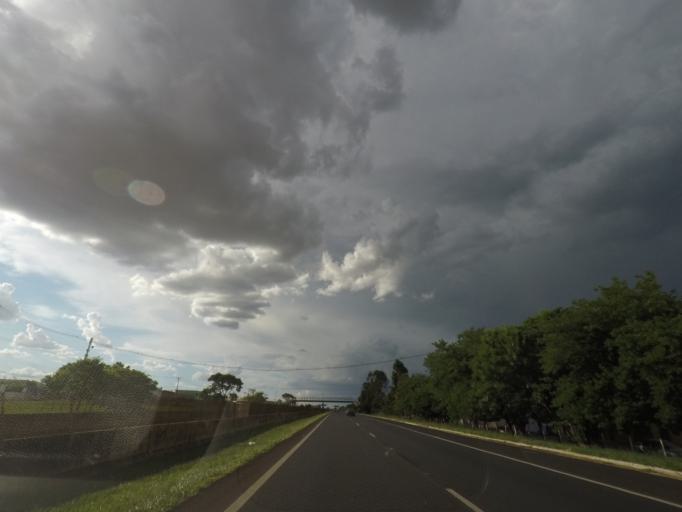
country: BR
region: Sao Paulo
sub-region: Ribeirao Preto
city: Ribeirao Preto
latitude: -21.1263
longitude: -47.7704
